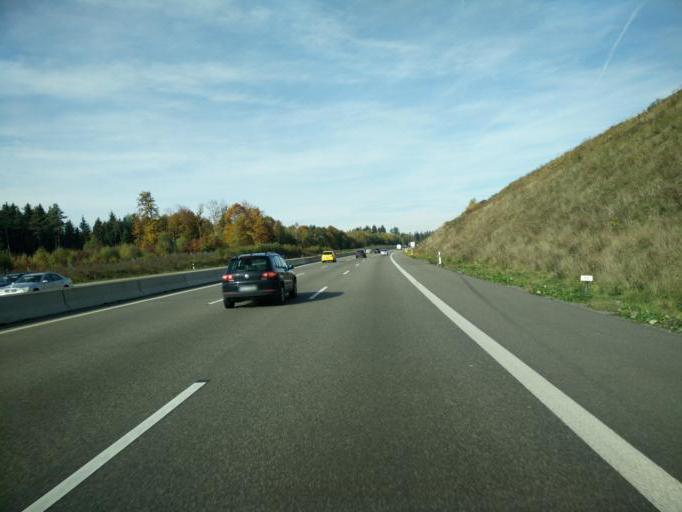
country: DE
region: Baden-Wuerttemberg
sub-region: Karlsruhe Region
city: Tiefenbronn
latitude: 48.8455
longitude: 8.8116
